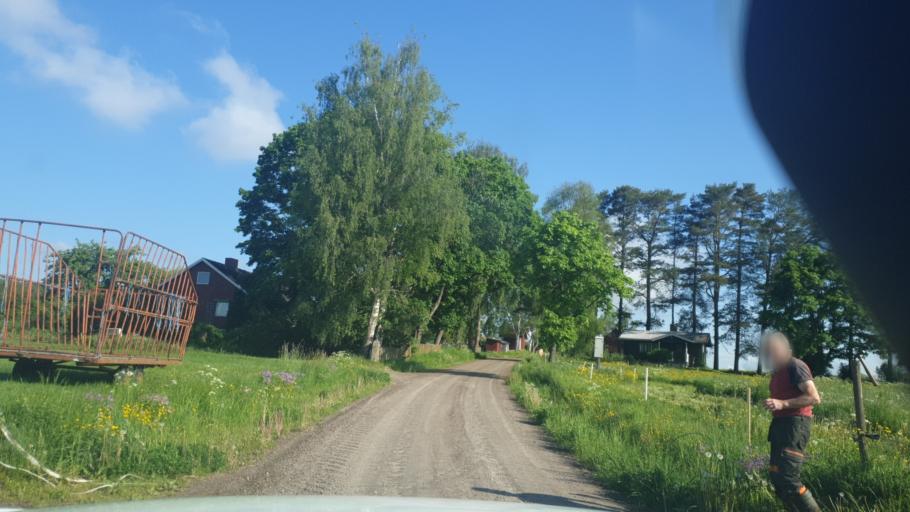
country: SE
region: Vaermland
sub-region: Eda Kommun
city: Charlottenberg
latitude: 59.7474
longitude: 12.1520
